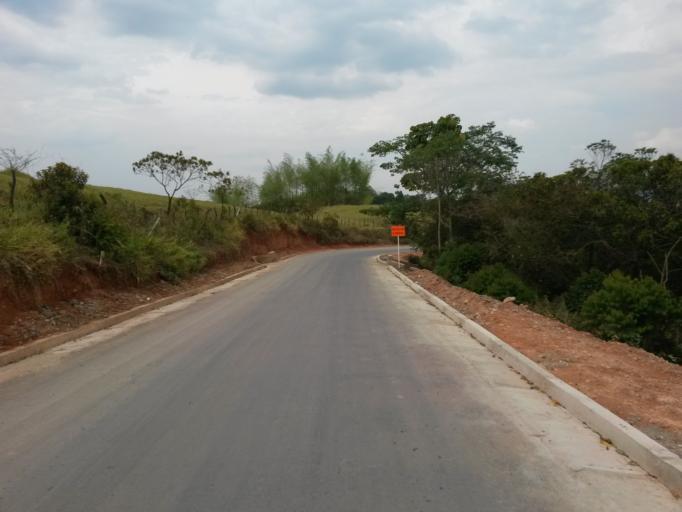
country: CO
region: Cauca
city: Buenos Aires
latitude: 3.0877
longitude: -76.6062
